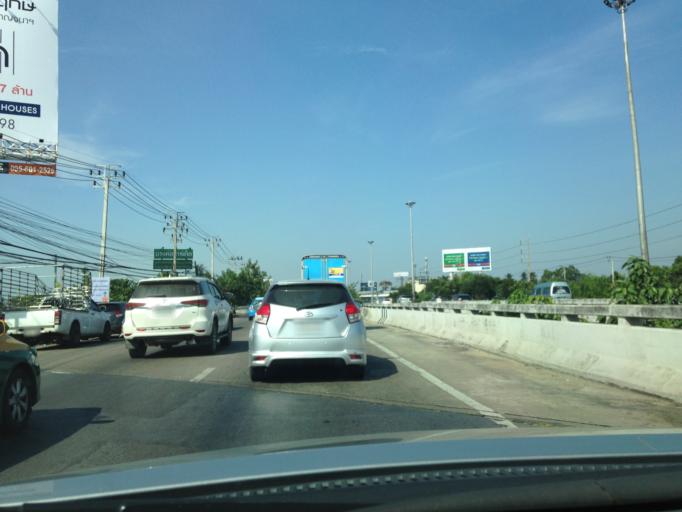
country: TH
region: Nonthaburi
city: Bang Yai
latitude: 13.8267
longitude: 100.4126
